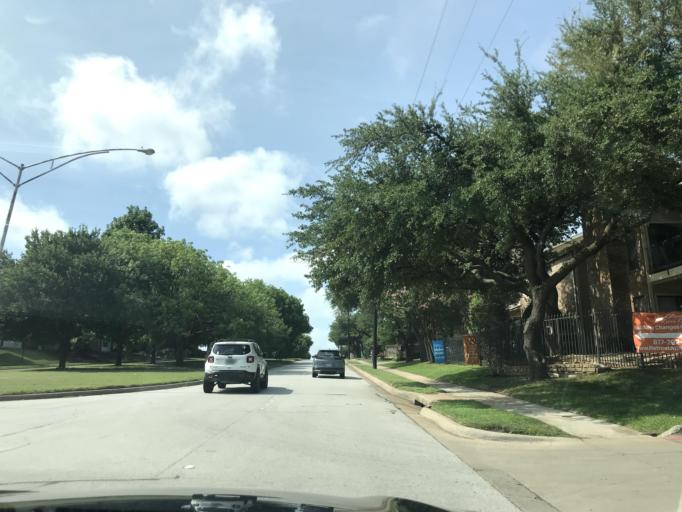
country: US
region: Texas
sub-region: Tarrant County
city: Benbrook
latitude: 32.6792
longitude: -97.4033
